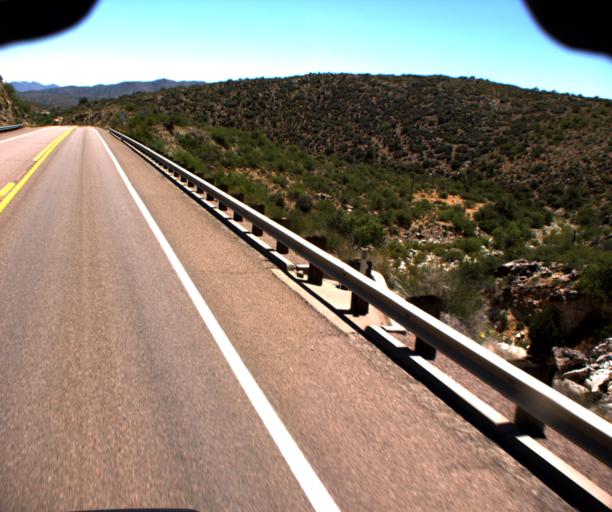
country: US
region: Arizona
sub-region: Yavapai County
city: Bagdad
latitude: 34.5512
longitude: -113.1523
